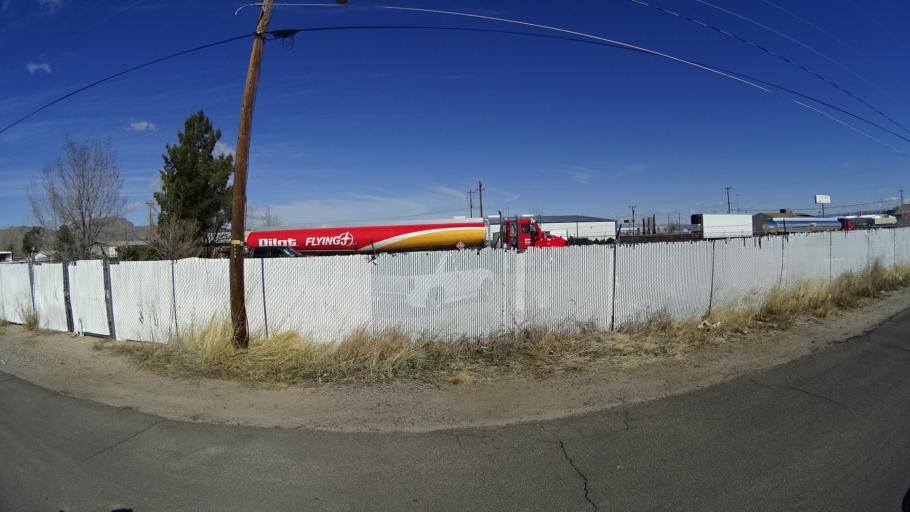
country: US
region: Arizona
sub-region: Mohave County
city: New Kingman-Butler
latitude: 35.2214
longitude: -114.0100
